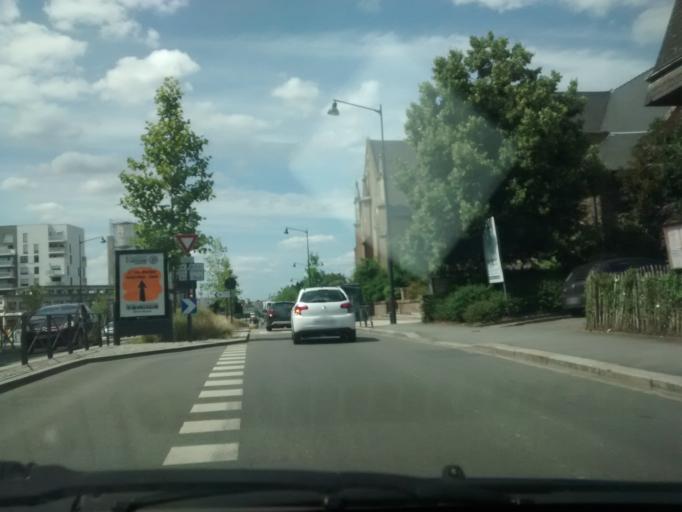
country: FR
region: Brittany
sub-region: Departement d'Ille-et-Vilaine
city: Rennes
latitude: 48.1025
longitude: -1.6609
